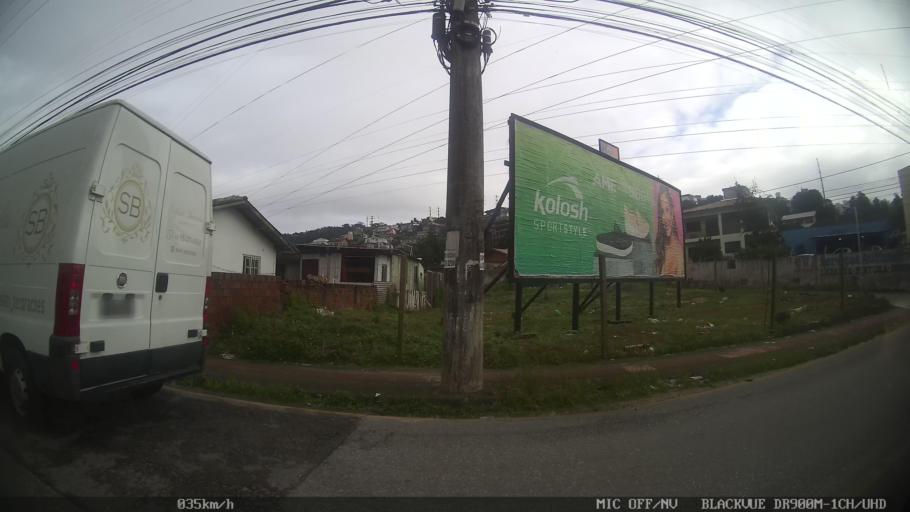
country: BR
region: Santa Catarina
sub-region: Sao Jose
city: Campinas
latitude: -27.5880
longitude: -48.6207
